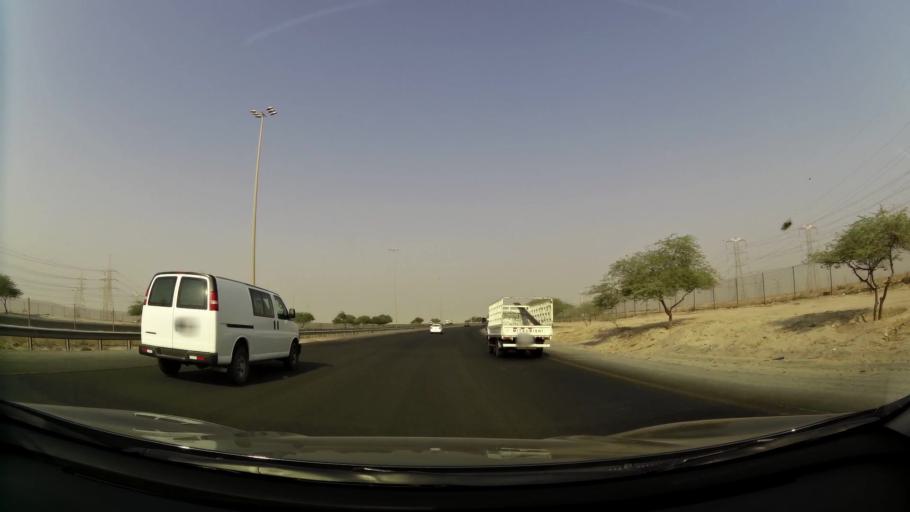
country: KW
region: Al Farwaniyah
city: Al Farwaniyah
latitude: 29.1887
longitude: 47.8866
